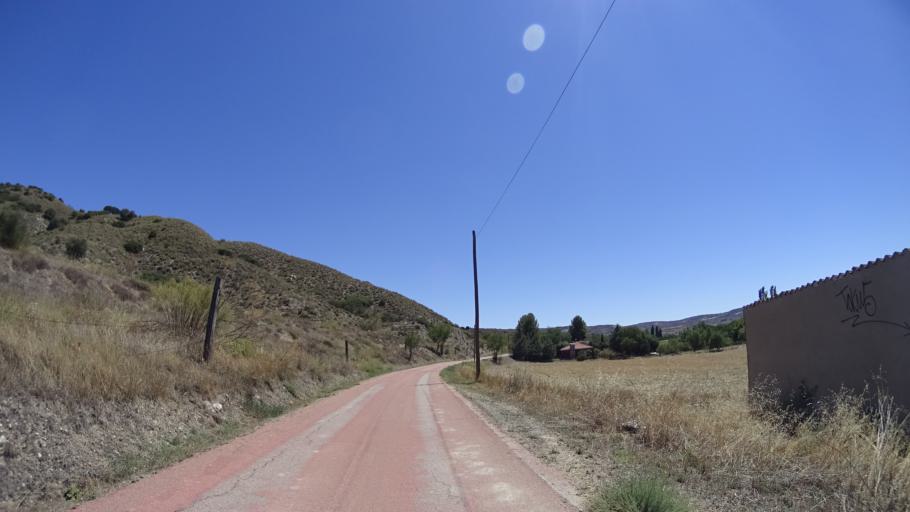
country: ES
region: Madrid
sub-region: Provincia de Madrid
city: Carabana
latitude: 40.2577
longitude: -3.2260
